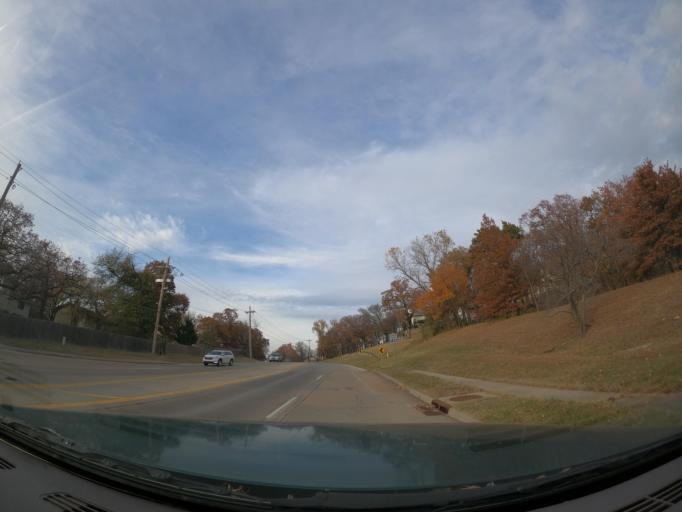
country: US
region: Oklahoma
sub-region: Tulsa County
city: Jenks
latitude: 36.0473
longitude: -95.9399
